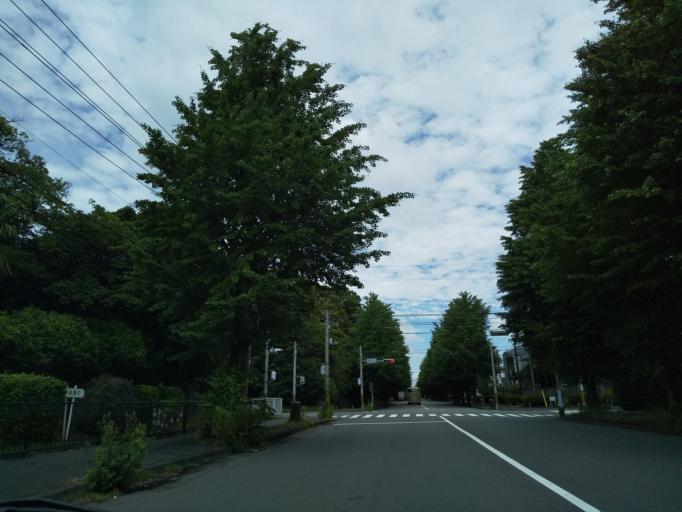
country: JP
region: Kanagawa
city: Zama
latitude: 35.5137
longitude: 139.3490
